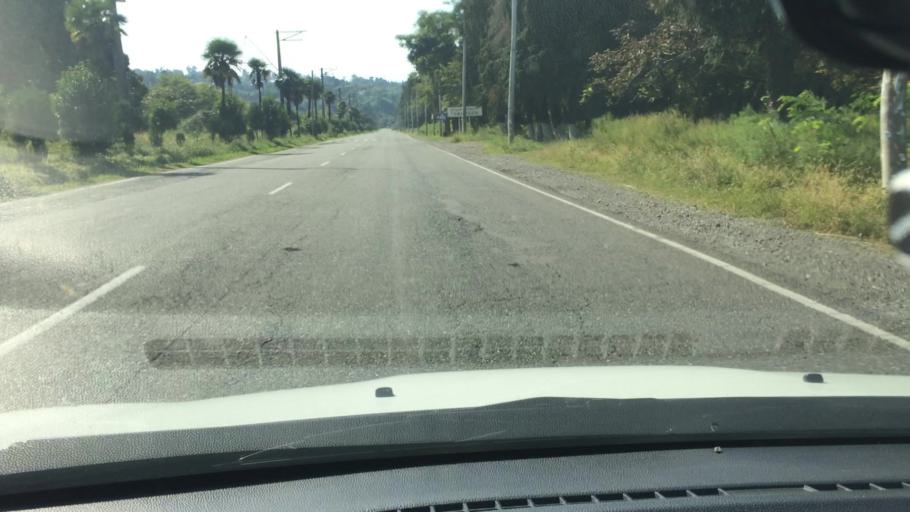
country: GE
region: Ajaria
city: Kobuleti
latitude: 41.7873
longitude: 41.7666
